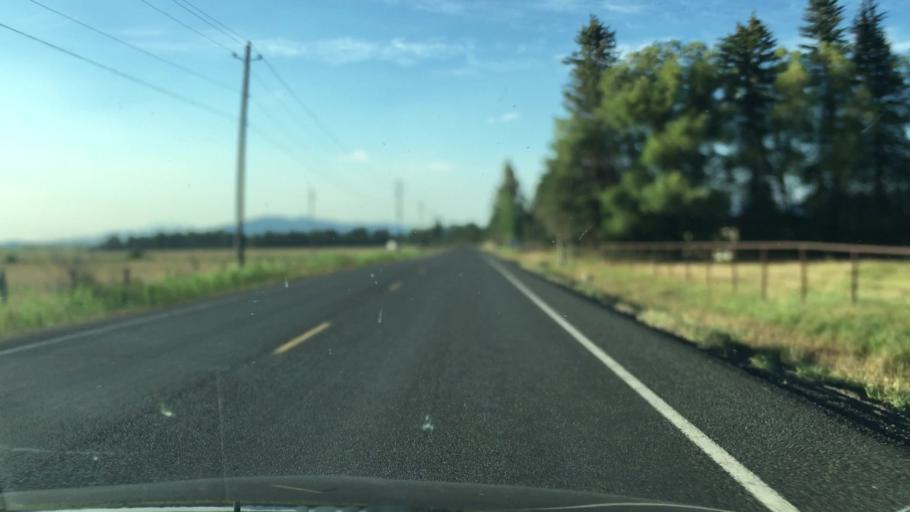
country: US
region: Idaho
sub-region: Valley County
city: McCall
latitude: 44.8169
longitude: -116.0781
